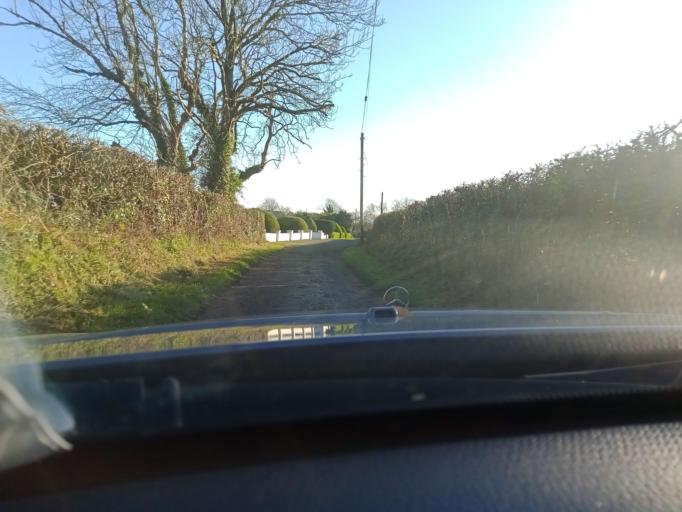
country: IE
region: Leinster
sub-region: Kilkenny
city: Mooncoin
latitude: 52.2962
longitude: -7.1874
